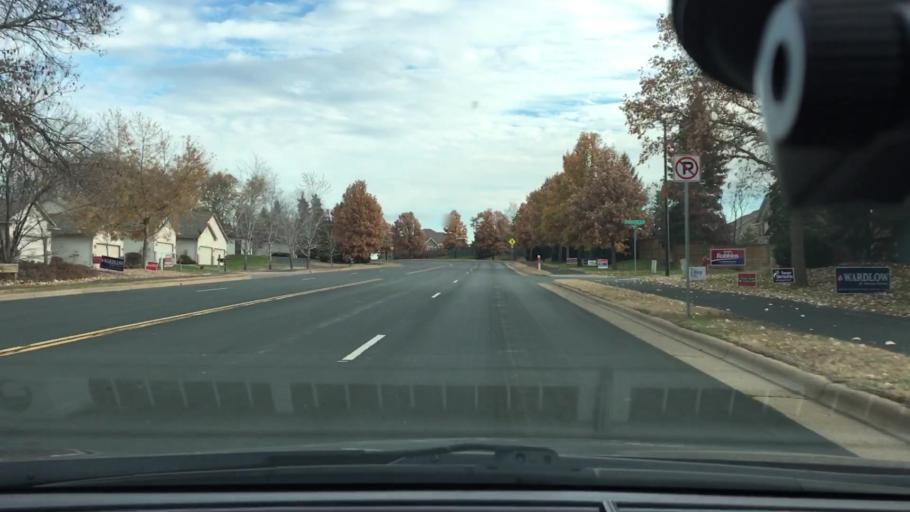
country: US
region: Minnesota
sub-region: Hennepin County
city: Maple Grove
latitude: 45.1044
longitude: -93.4774
